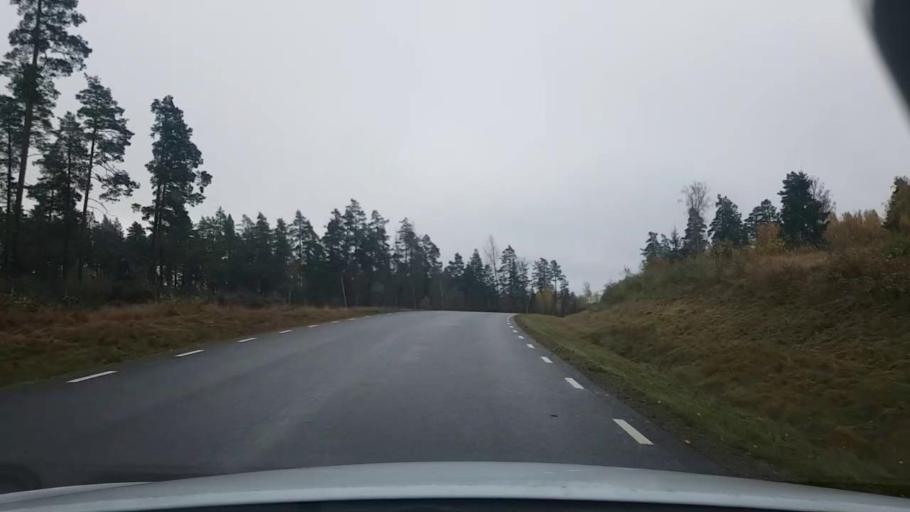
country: SE
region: Vaestra Goetaland
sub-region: Karlsborgs Kommun
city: Karlsborg
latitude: 58.6889
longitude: 14.5003
